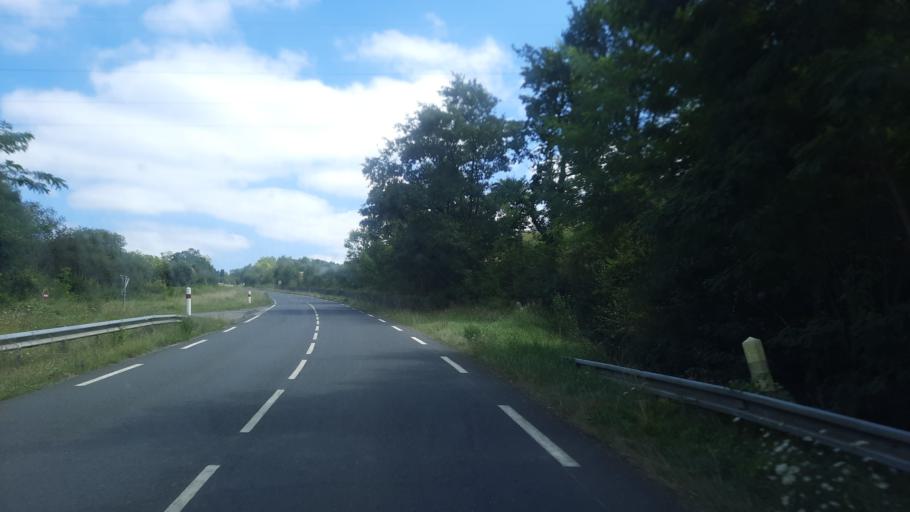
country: FR
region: Midi-Pyrenees
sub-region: Departement de la Haute-Garonne
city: Boulogne-sur-Gesse
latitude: 43.2912
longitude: 0.6322
